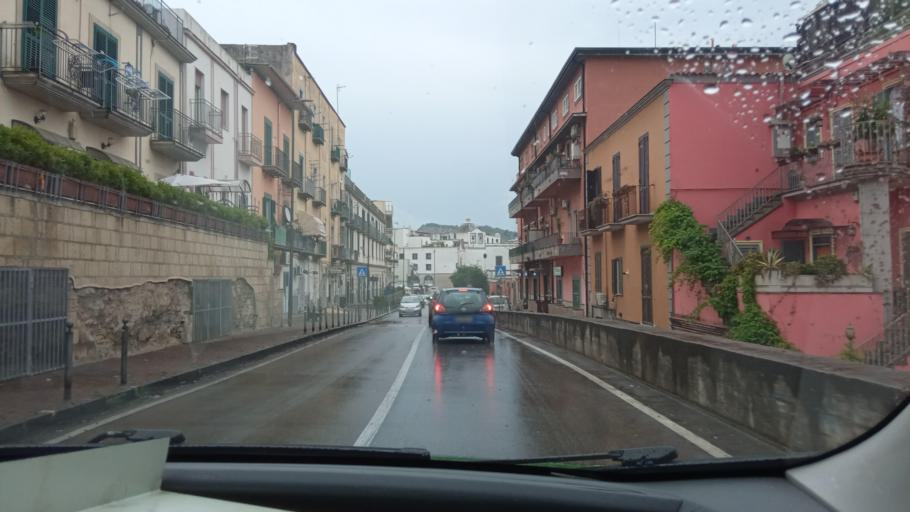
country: IT
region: Campania
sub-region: Provincia di Napoli
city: Pozzuoli
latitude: 40.8313
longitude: 14.1178
